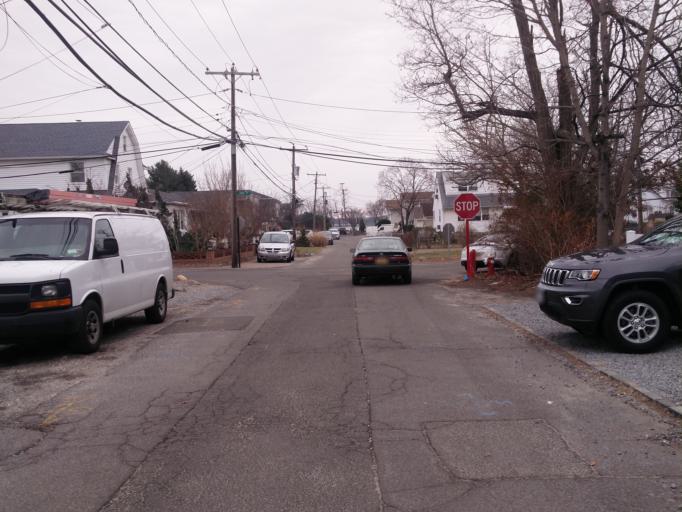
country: US
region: New York
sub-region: Nassau County
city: Bayville
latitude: 40.9070
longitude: -73.5439
